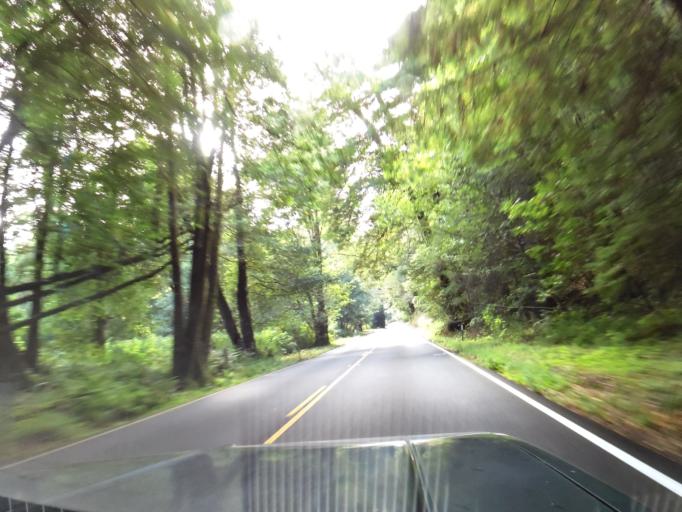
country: US
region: California
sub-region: Mendocino County
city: Fort Bragg
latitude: 39.1732
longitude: -123.6709
